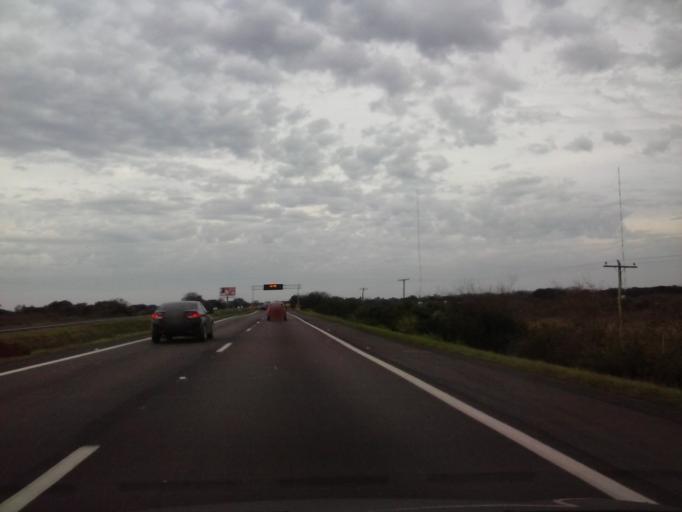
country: BR
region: Rio Grande do Sul
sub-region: Porto Alegre
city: Porto Alegre
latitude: -29.9986
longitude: -51.2933
